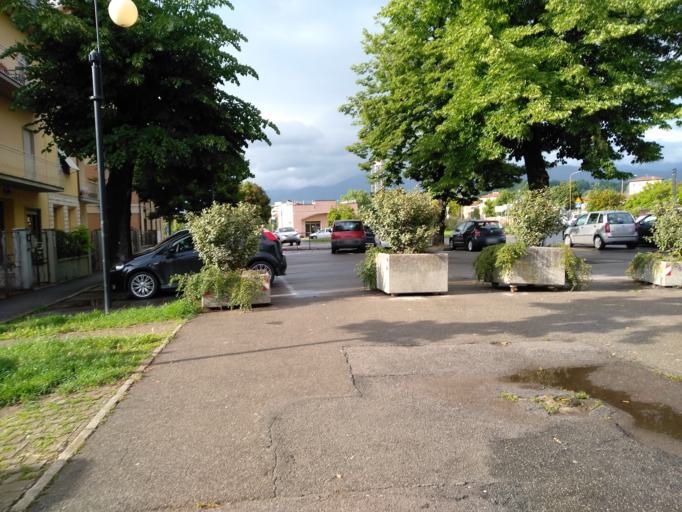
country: IT
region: Tuscany
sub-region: Province of Arezzo
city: San Giovanni Valdarno
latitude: 43.5654
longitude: 11.5341
